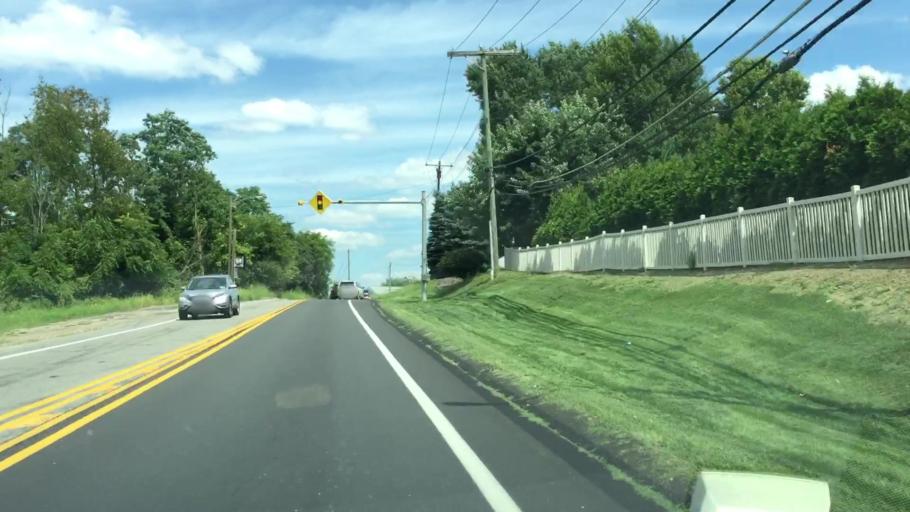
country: US
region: Pennsylvania
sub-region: Allegheny County
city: Bethel Park
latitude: 40.3371
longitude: -80.0194
